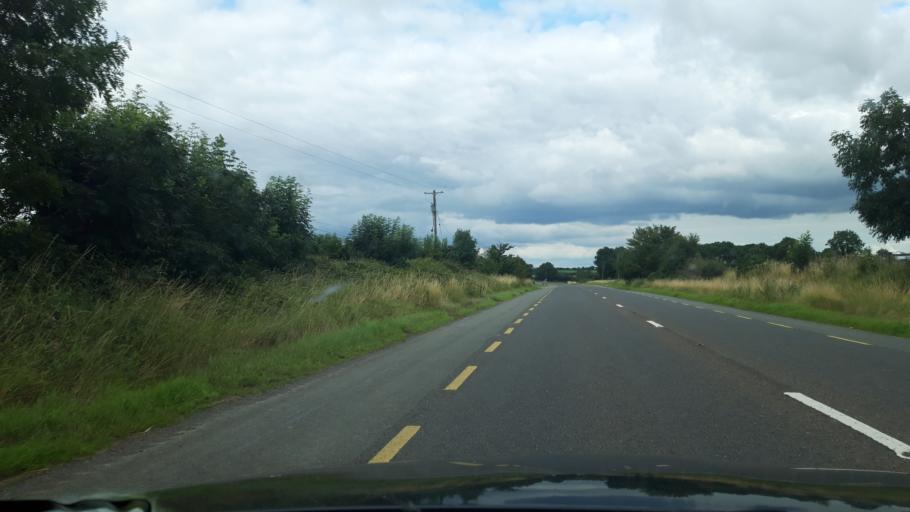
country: IE
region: Leinster
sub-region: County Carlow
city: Bagenalstown
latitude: 52.6661
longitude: -7.0309
